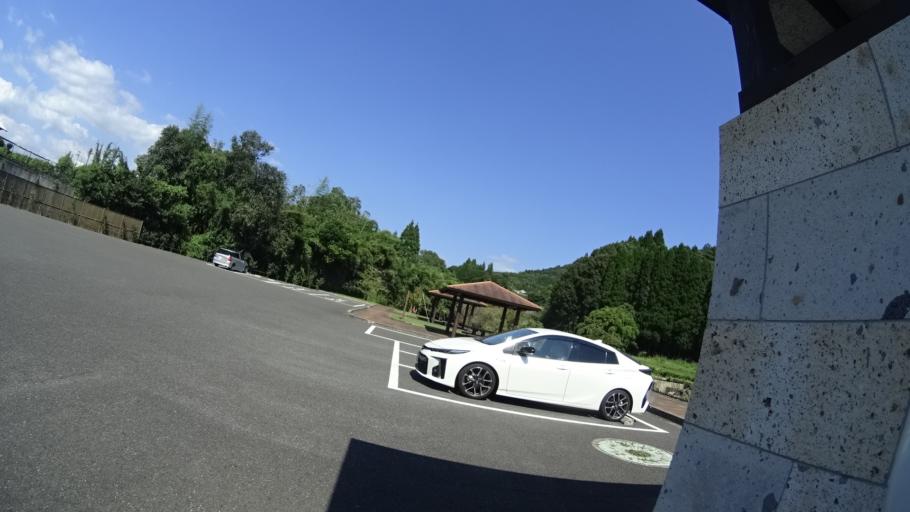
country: JP
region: Kagoshima
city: Kajiki
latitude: 31.7546
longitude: 130.6752
